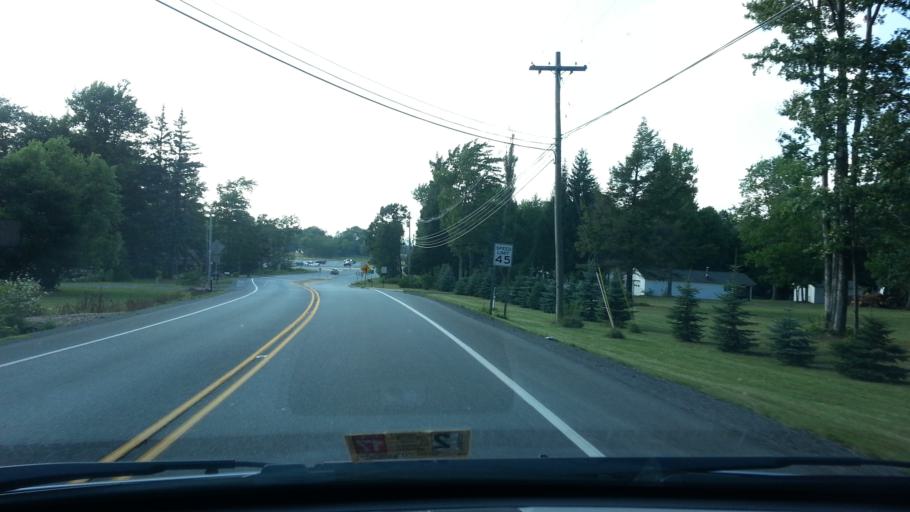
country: US
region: Pennsylvania
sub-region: Elk County
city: Saint Marys
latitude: 41.3642
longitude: -78.5543
